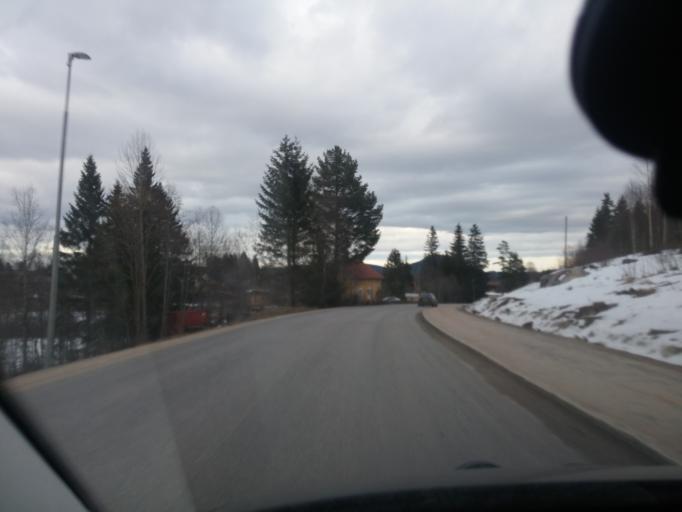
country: SE
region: Gaevleborg
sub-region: Ljusdals Kommun
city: Jaervsoe
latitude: 61.7247
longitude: 16.1566
